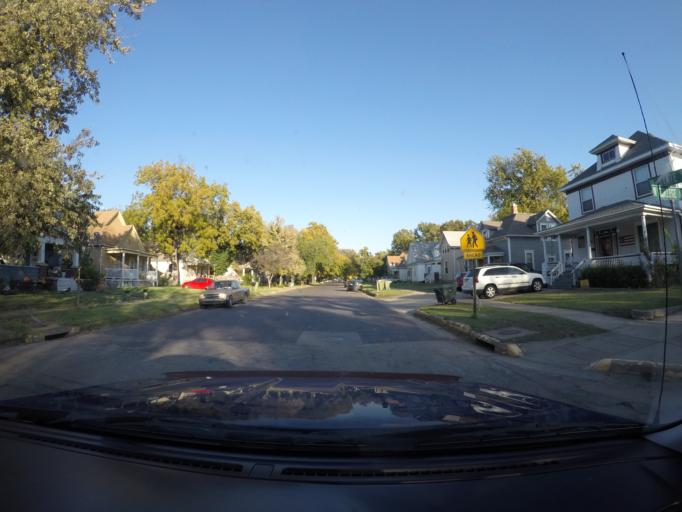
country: US
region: Kansas
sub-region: Saline County
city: Salina
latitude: 38.8416
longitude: -97.6198
